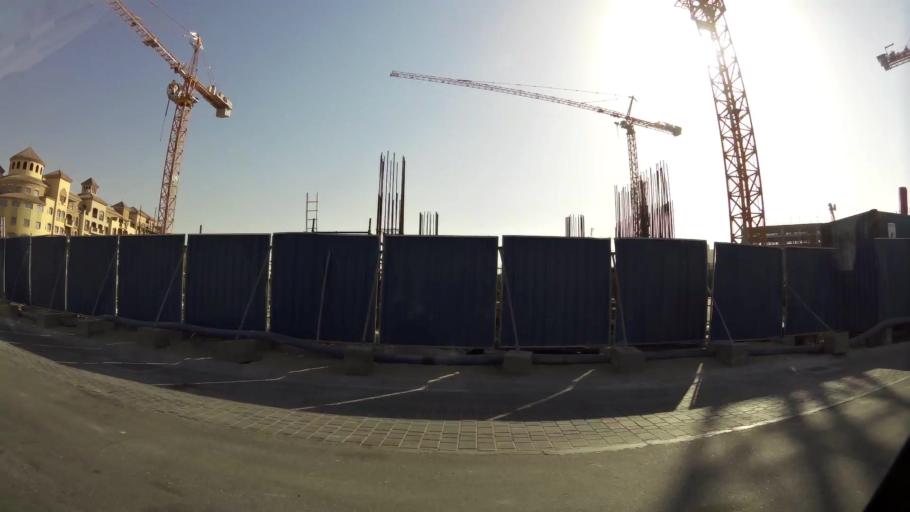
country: AE
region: Dubai
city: Dubai
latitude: 25.0658
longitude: 55.2166
